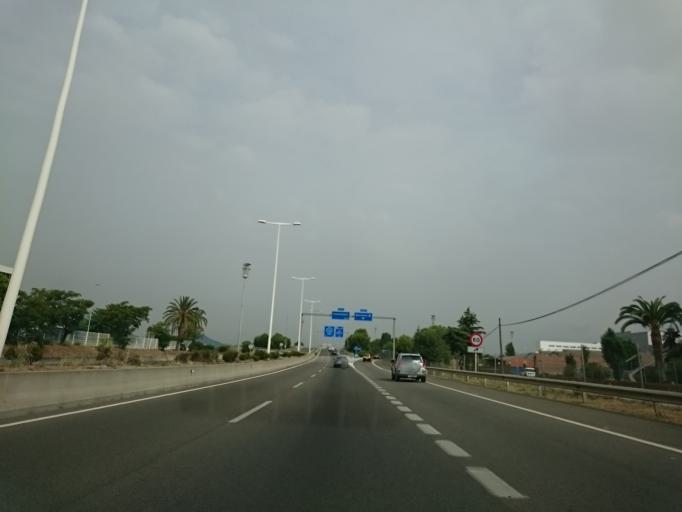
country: ES
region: Catalonia
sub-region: Provincia de Barcelona
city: El Prat de Llobregat
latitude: 41.3190
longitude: 2.0768
